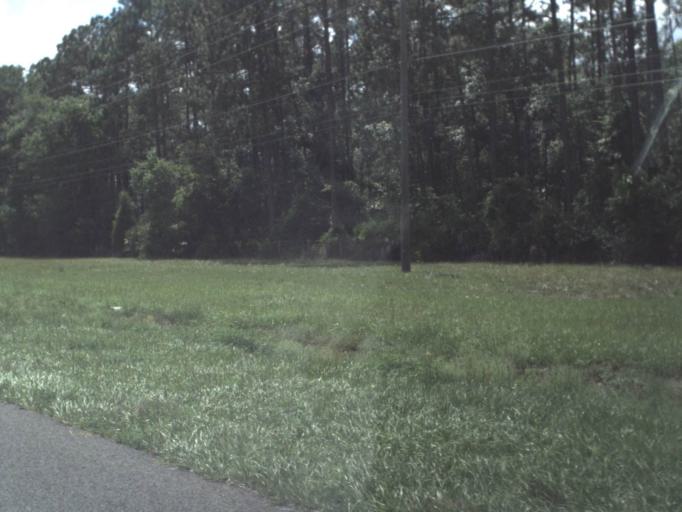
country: US
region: Florida
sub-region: Duval County
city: Baldwin
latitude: 30.2428
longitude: -81.8980
